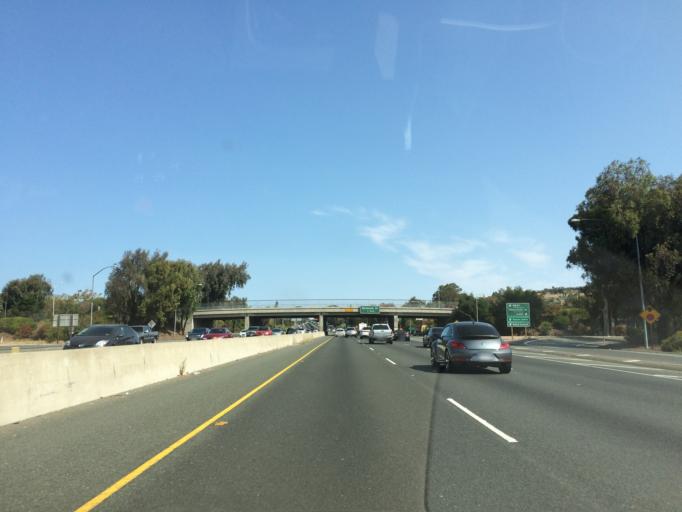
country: US
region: California
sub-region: Solano County
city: Vallejo
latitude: 38.1080
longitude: -122.2296
